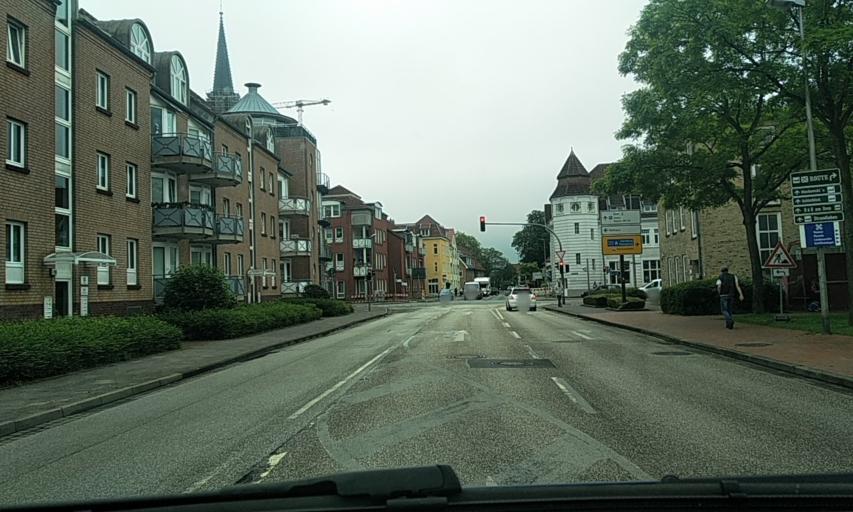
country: DE
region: Schleswig-Holstein
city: Schleswig
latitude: 54.5155
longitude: 9.5666
